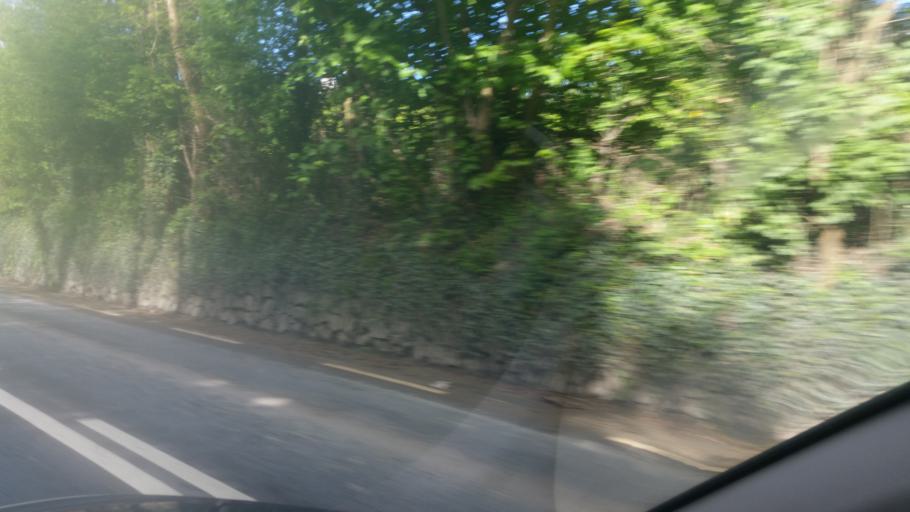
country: IE
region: Leinster
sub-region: Loch Garman
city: Enniscorthy
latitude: 52.5086
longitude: -6.5679
